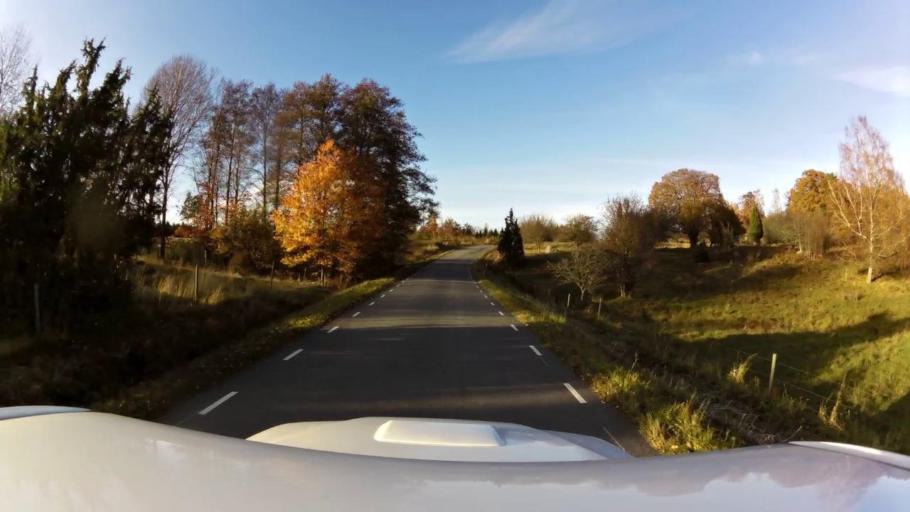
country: SE
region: OEstergoetland
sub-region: Linkopings Kommun
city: Sturefors
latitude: 58.2673
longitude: 15.6656
